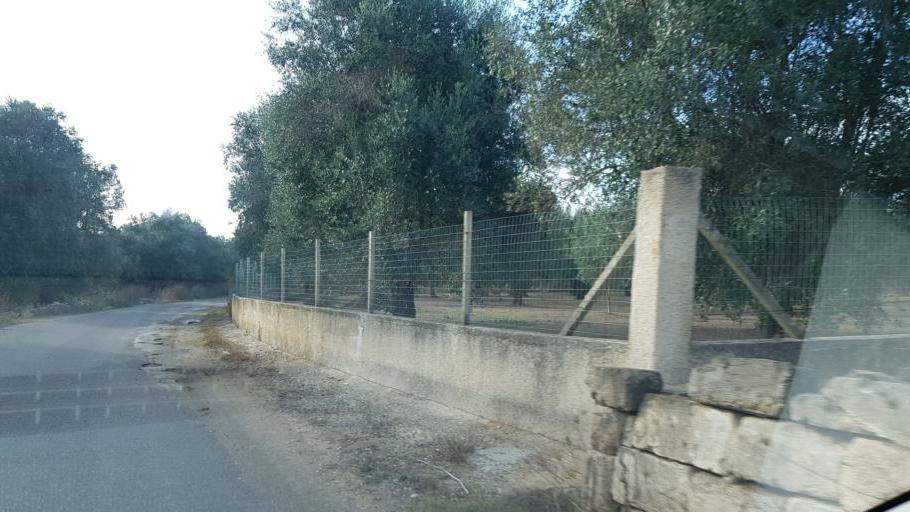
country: IT
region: Apulia
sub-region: Provincia di Brindisi
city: Oria
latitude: 40.5011
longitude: 17.6722
